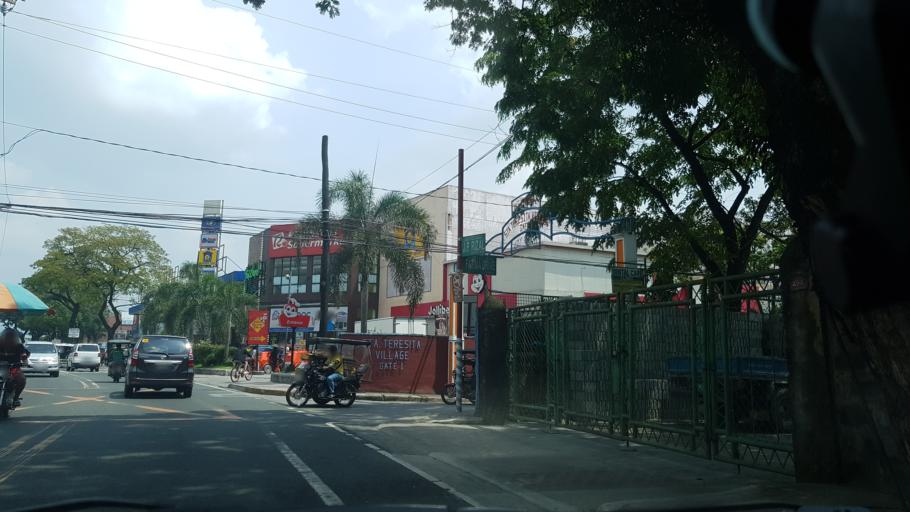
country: PH
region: Metro Manila
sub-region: Marikina
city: Calumpang
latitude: 14.6452
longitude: 121.0963
